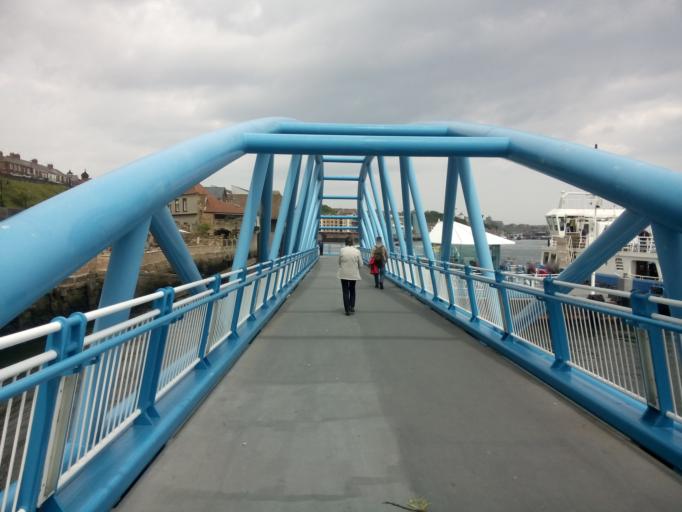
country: GB
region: England
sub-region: South Tyneside
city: South Shields
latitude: 55.0034
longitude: -1.4441
